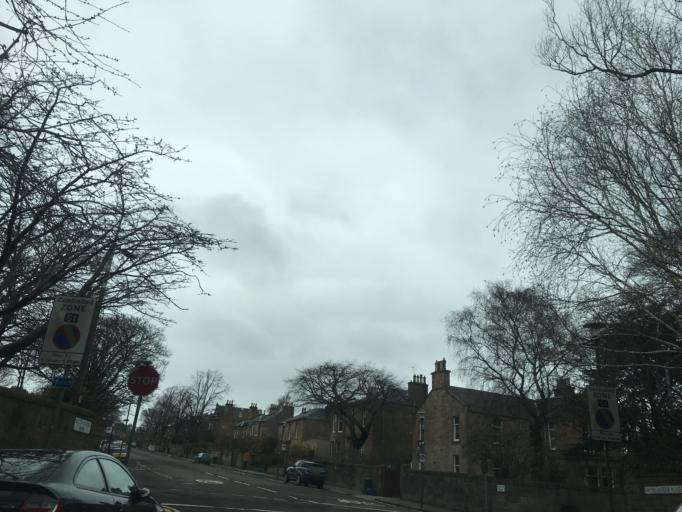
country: GB
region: Scotland
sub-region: Edinburgh
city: Edinburgh
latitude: 55.9320
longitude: -3.1829
